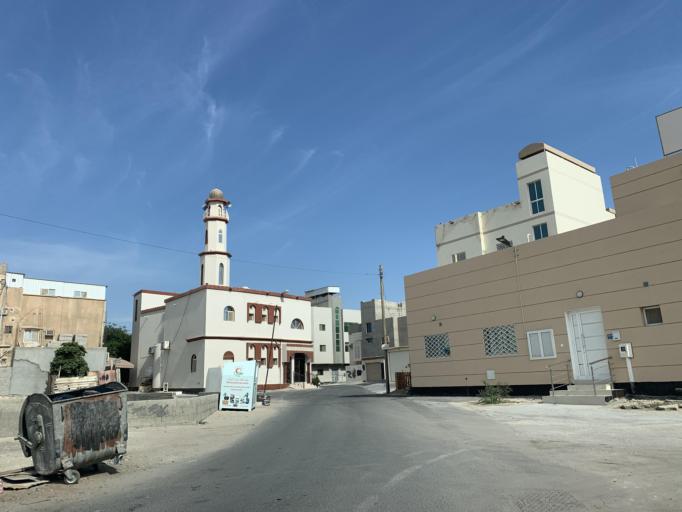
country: BH
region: Central Governorate
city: Madinat Hamad
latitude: 26.1246
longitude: 50.4754
